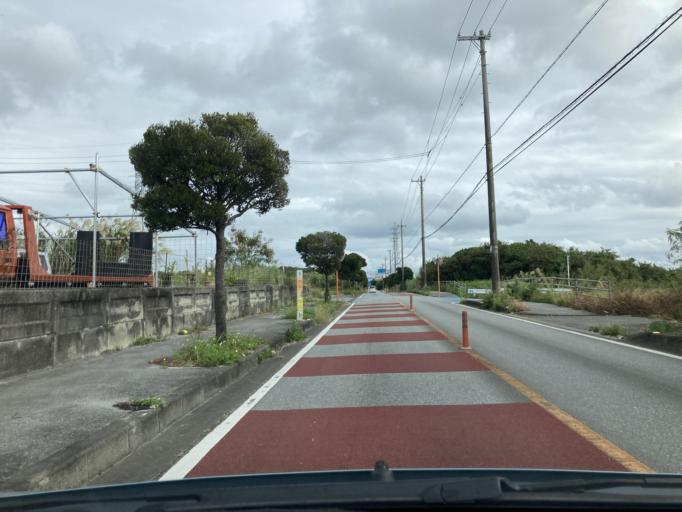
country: JP
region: Okinawa
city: Itoman
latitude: 26.1197
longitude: 127.6852
